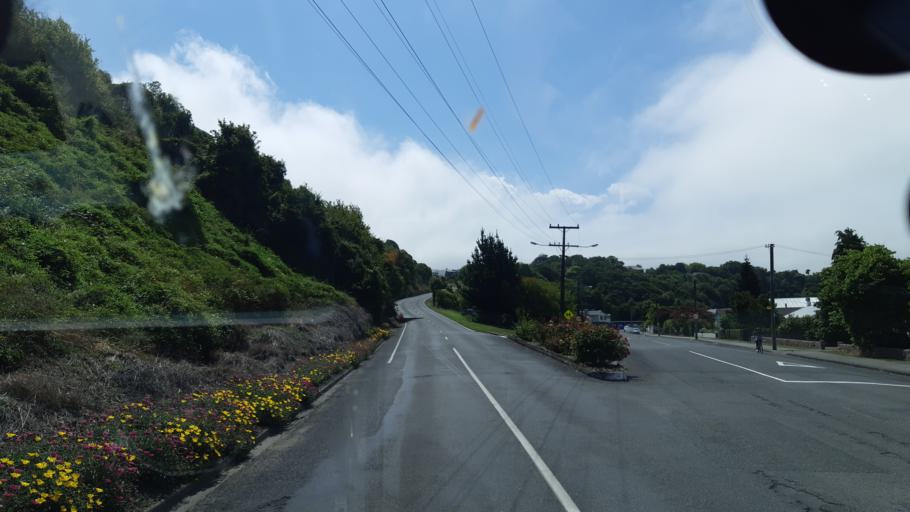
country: NZ
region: Canterbury
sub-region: Kaikoura District
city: Kaikoura
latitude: -42.4094
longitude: 173.6838
